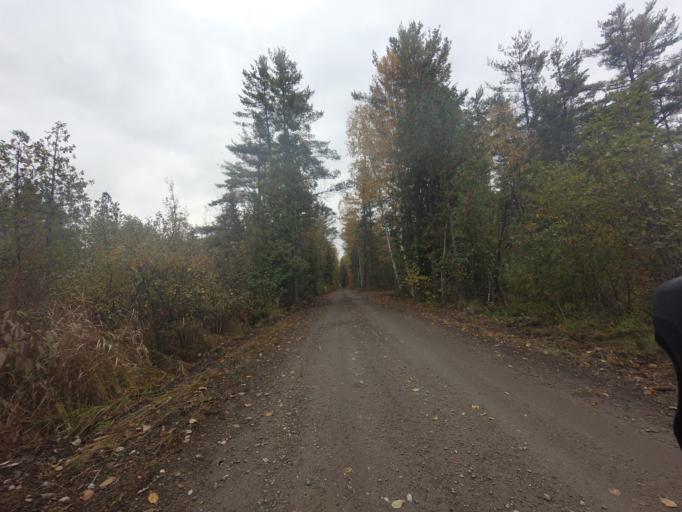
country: CA
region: Ontario
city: Renfrew
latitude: 45.1849
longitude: -76.6855
